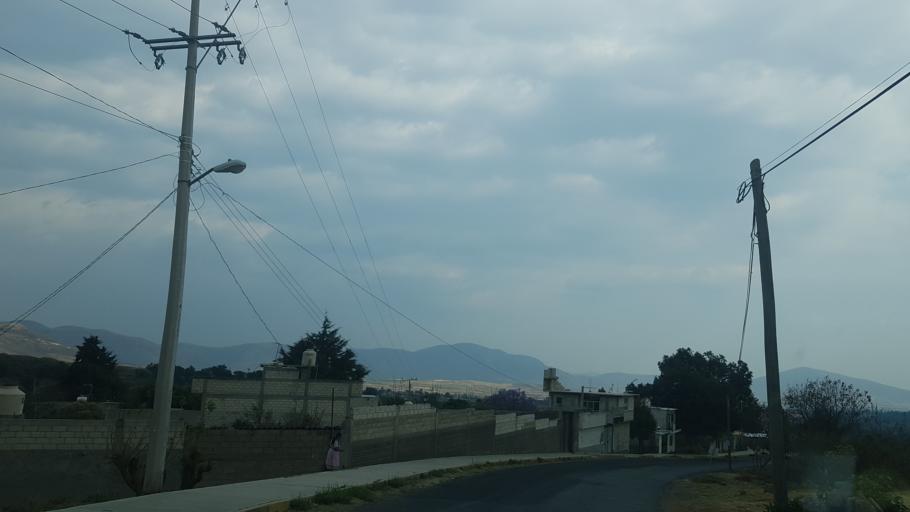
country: MX
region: Puebla
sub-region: Santa Isabel Cholula
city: San Martin Tlamapa
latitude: 18.9752
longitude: -98.3950
